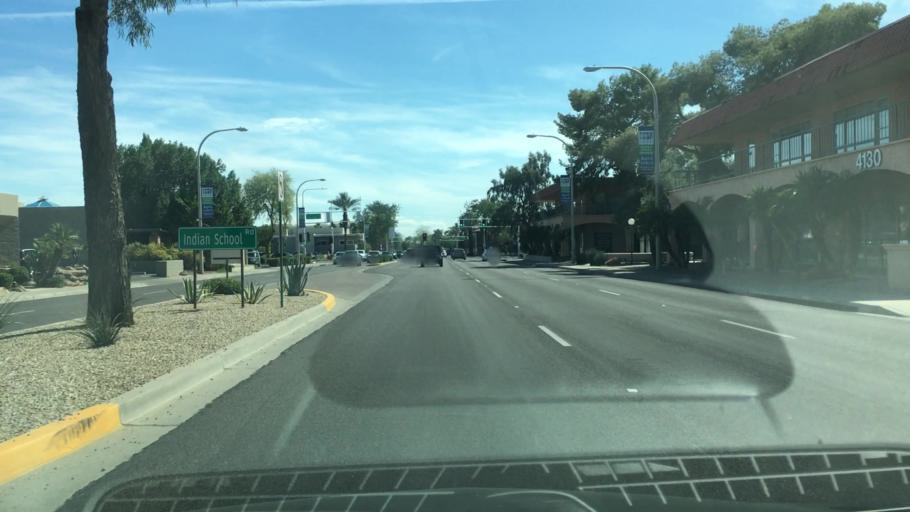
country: US
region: Arizona
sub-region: Maricopa County
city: Scottsdale
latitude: 33.4961
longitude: -111.9304
